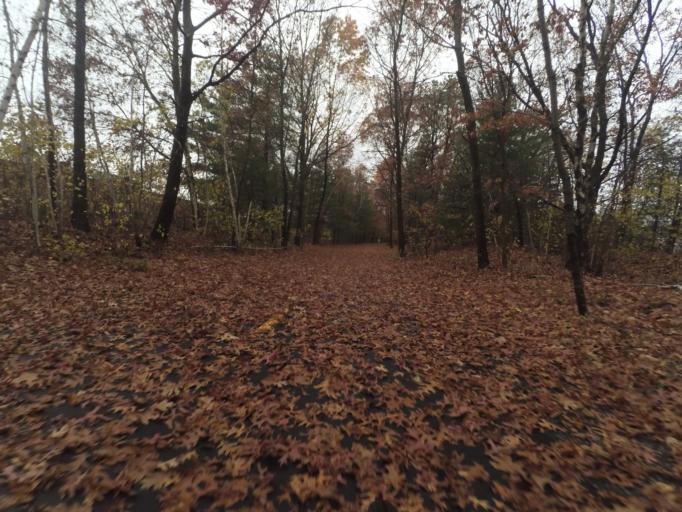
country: US
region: Massachusetts
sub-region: Middlesex County
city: Bedford
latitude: 42.4716
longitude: -71.2583
